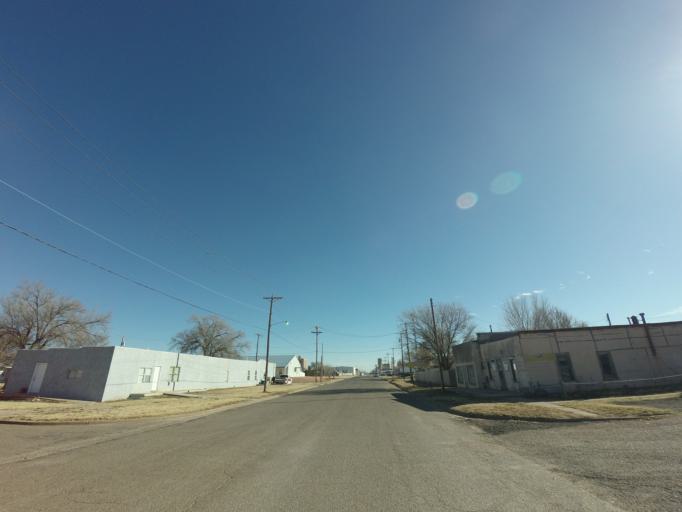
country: US
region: New Mexico
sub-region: Curry County
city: Clovis
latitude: 34.3986
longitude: -103.2118
